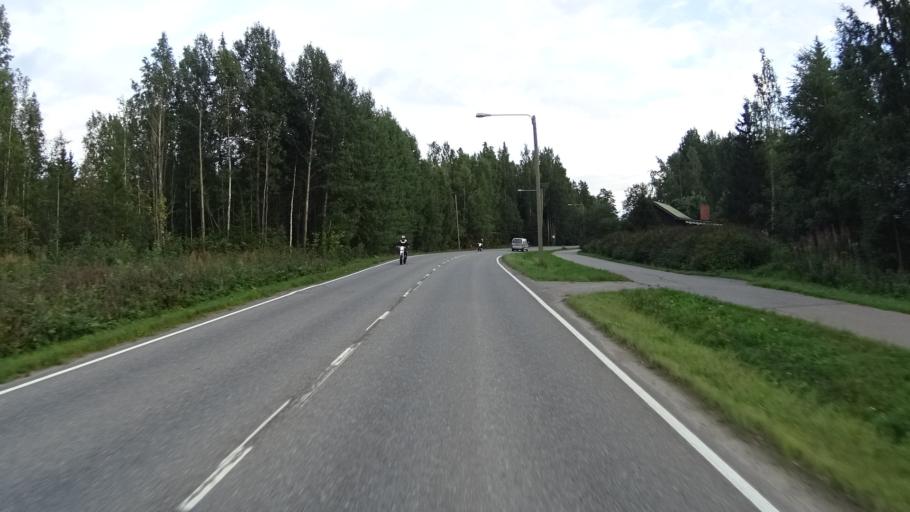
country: FI
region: Uusimaa
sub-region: Helsinki
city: Kilo
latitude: 60.3243
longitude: 24.8685
